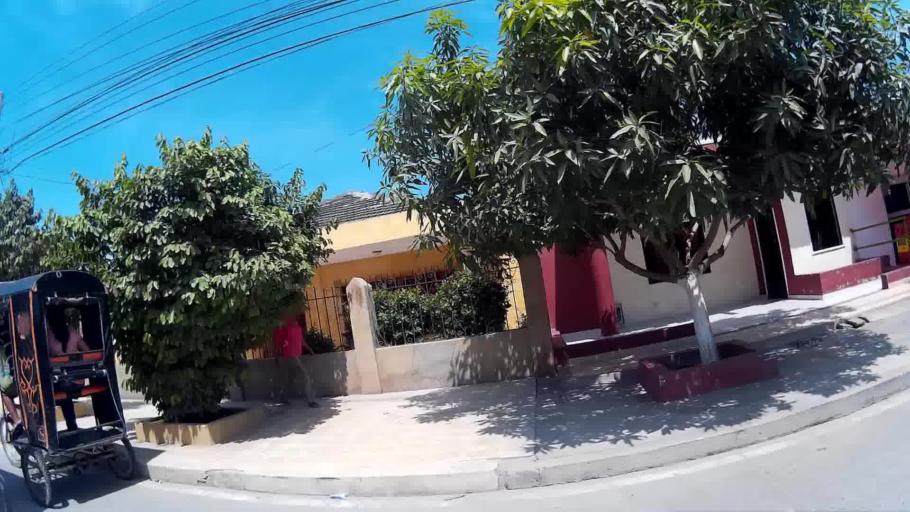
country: CO
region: Magdalena
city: Cienaga
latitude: 11.0114
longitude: -74.2451
